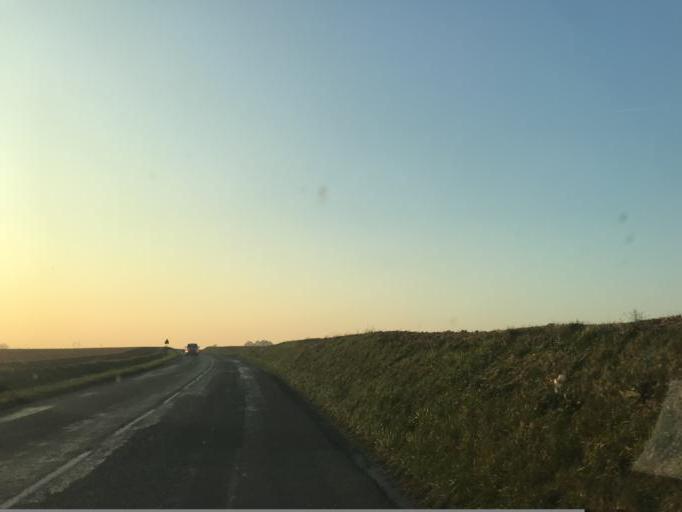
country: FR
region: Ile-de-France
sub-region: Departement de Seine-et-Marne
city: Juilly
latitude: 49.0137
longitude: 2.7439
